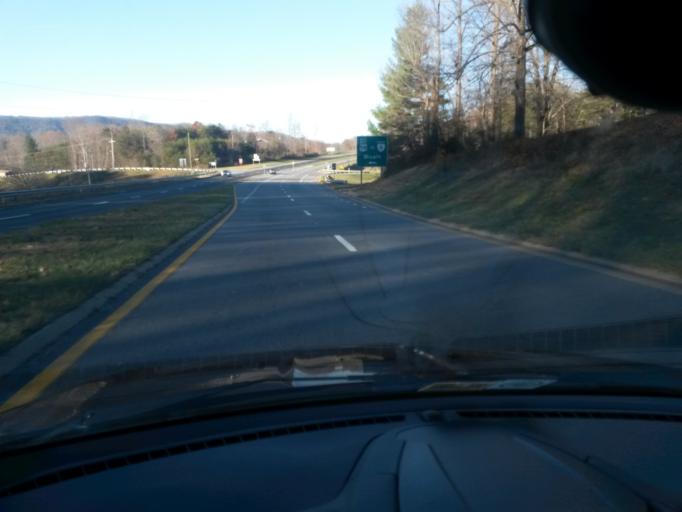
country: US
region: Virginia
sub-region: Patrick County
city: Stuart
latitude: 36.6463
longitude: -80.2604
